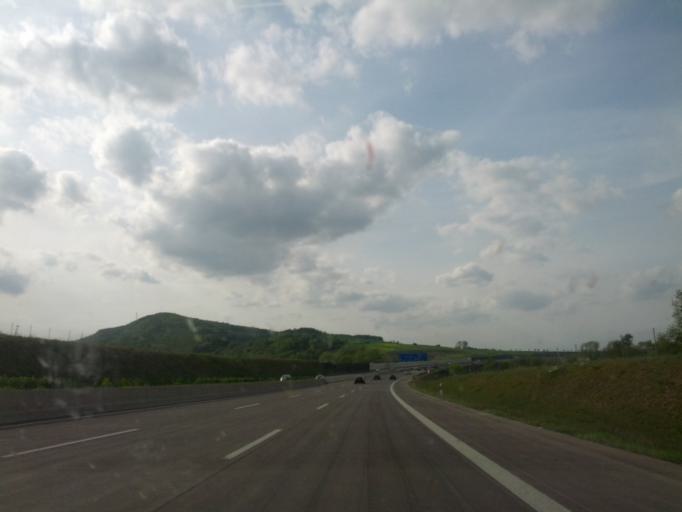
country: DE
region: Thuringia
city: Mechterstadt
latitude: 50.9400
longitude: 10.4923
